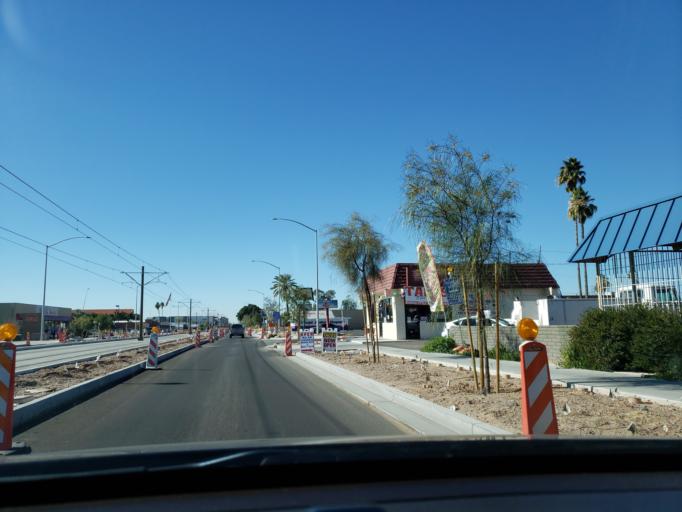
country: US
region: Arizona
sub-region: Maricopa County
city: Mesa
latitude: 33.4152
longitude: -111.8077
